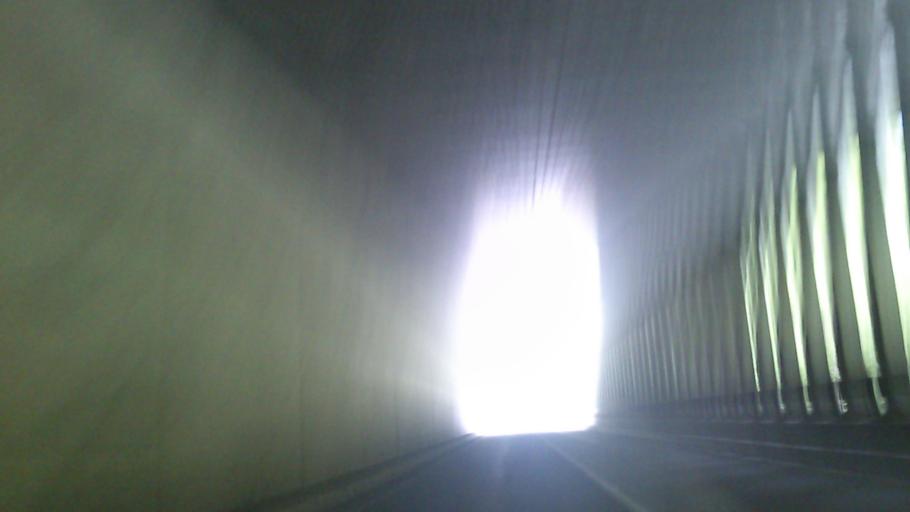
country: JP
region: Hokkaido
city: Kamikawa
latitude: 43.7381
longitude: 142.9386
